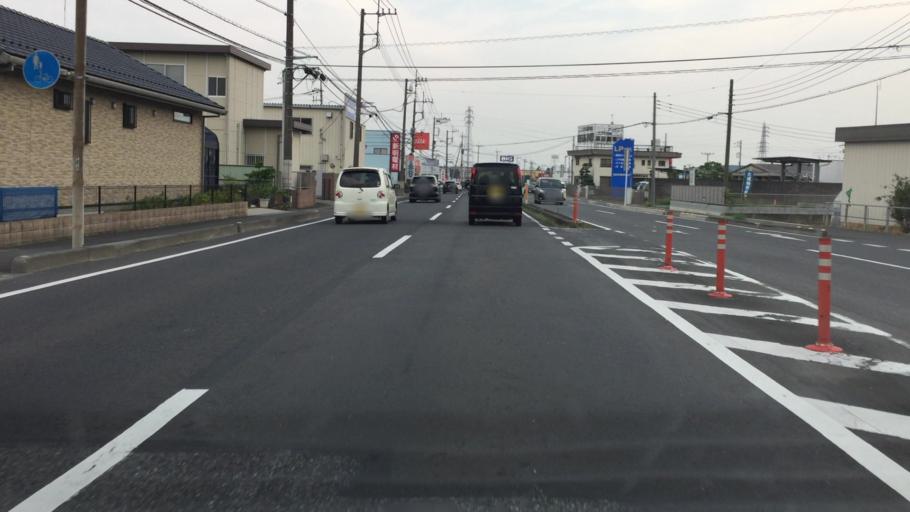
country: JP
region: Tochigi
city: Tochigi
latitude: 36.3518
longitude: 139.7104
